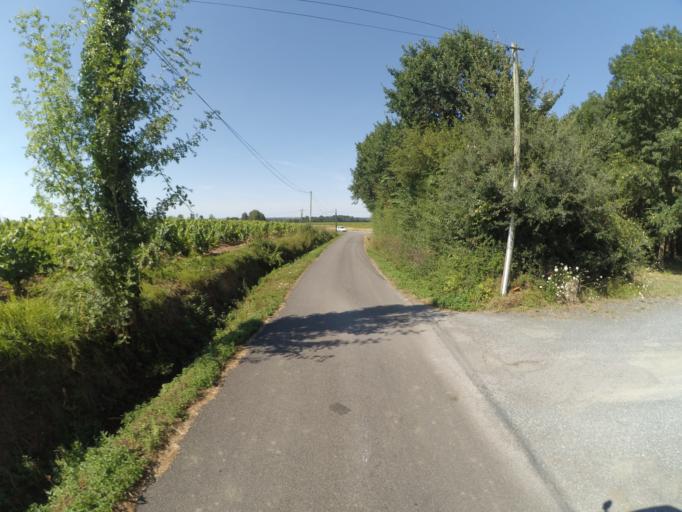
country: FR
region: Pays de la Loire
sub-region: Departement de la Loire-Atlantique
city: La Chapelle-Heulin
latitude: 47.1626
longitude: -1.3353
